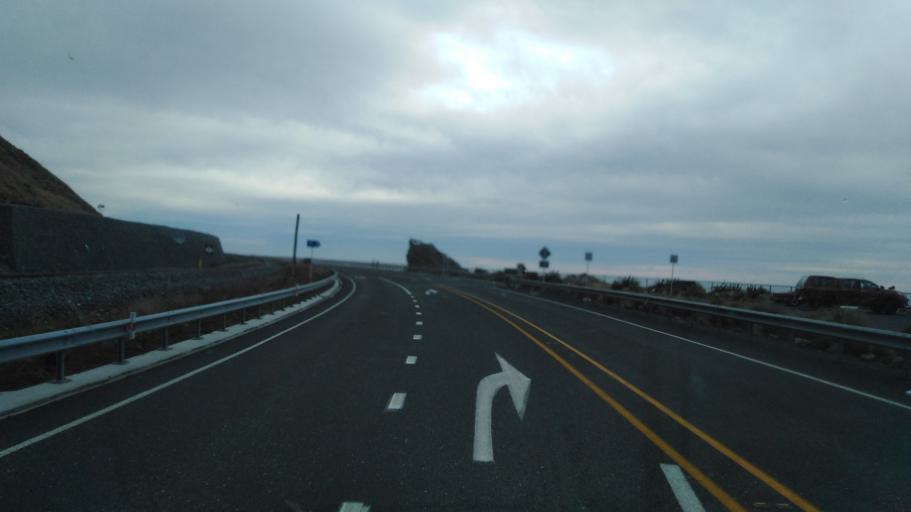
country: NZ
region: Canterbury
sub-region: Kaikoura District
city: Kaikoura
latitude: -42.2442
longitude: 173.8334
